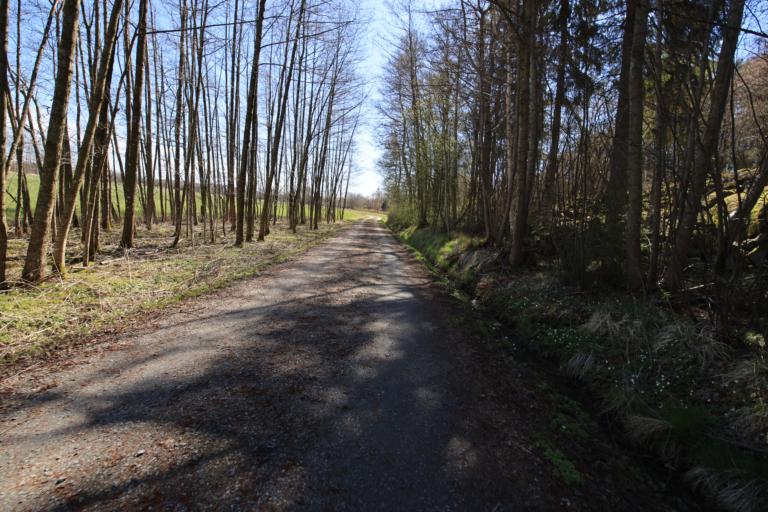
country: SE
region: Halland
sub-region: Varbergs Kommun
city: Varberg
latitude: 57.1626
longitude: 12.2495
